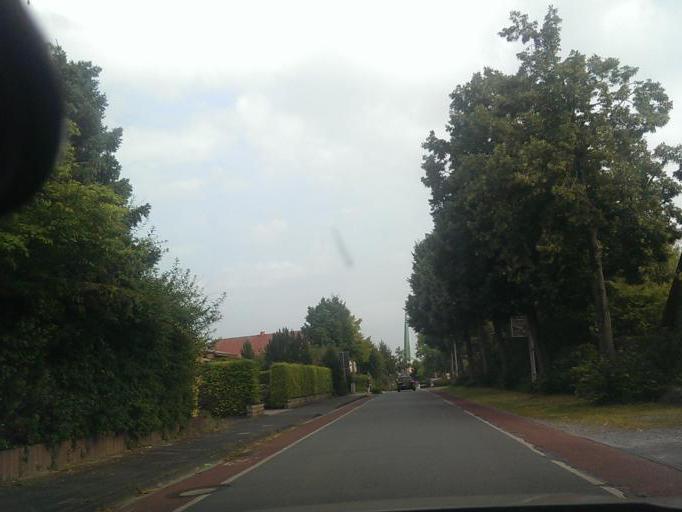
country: DE
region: North Rhine-Westphalia
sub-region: Regierungsbezirk Detmold
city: Delbruck
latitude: 51.7678
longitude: 8.5587
